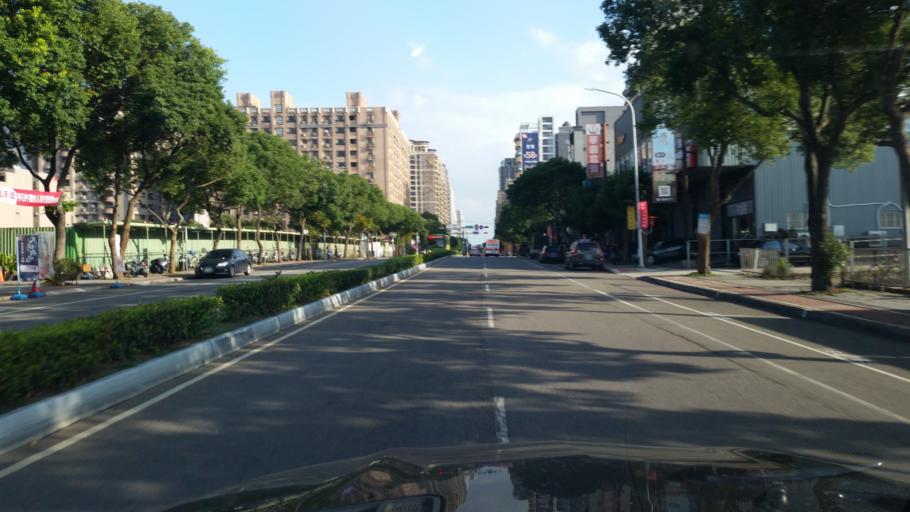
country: TW
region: Taiwan
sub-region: Taoyuan
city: Taoyuan
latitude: 25.0806
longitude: 121.3694
